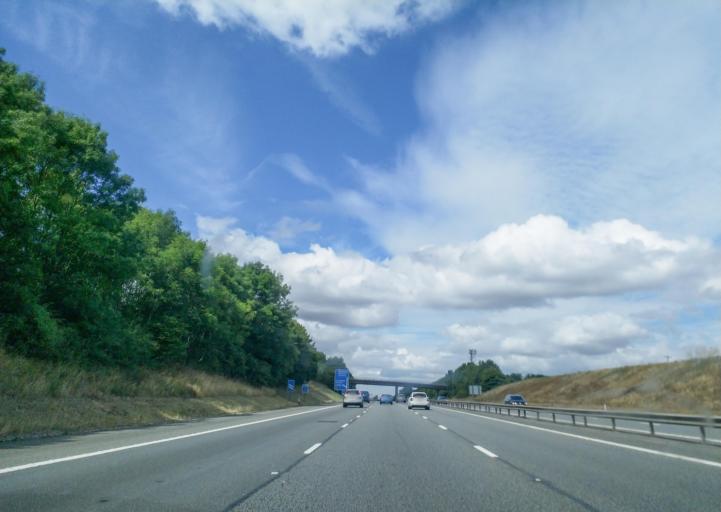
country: GB
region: England
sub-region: Warwickshire
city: Warwick
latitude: 52.2368
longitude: -1.5447
